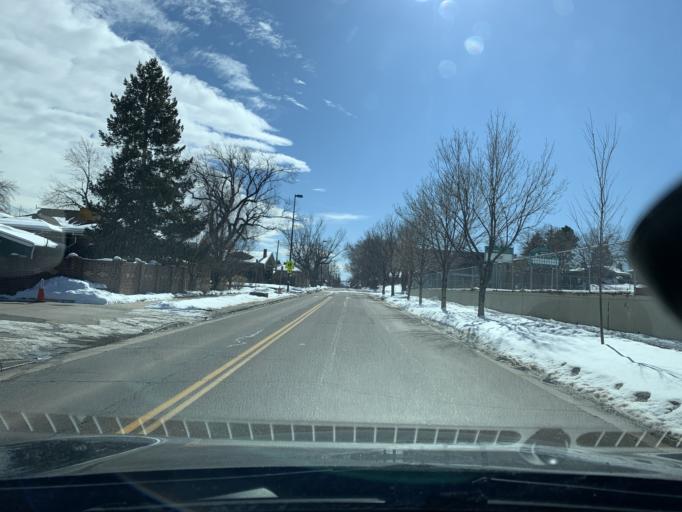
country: US
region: Colorado
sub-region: Adams County
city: Berkley
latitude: 39.7727
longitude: -105.0300
